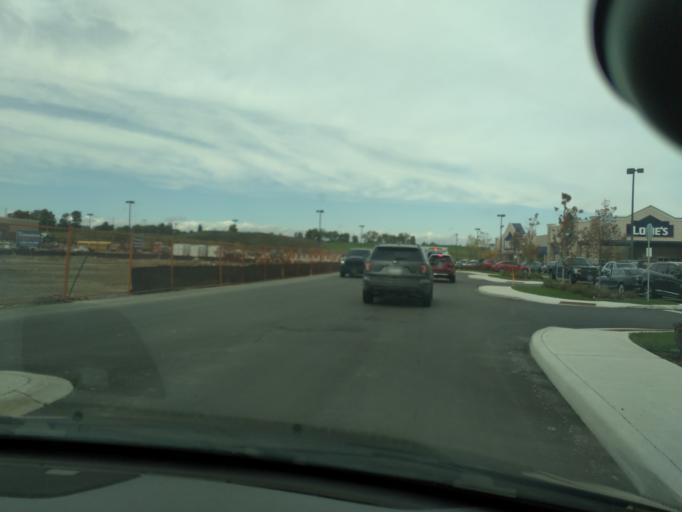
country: CA
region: Ontario
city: Newmarket
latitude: 44.0751
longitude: -79.4818
